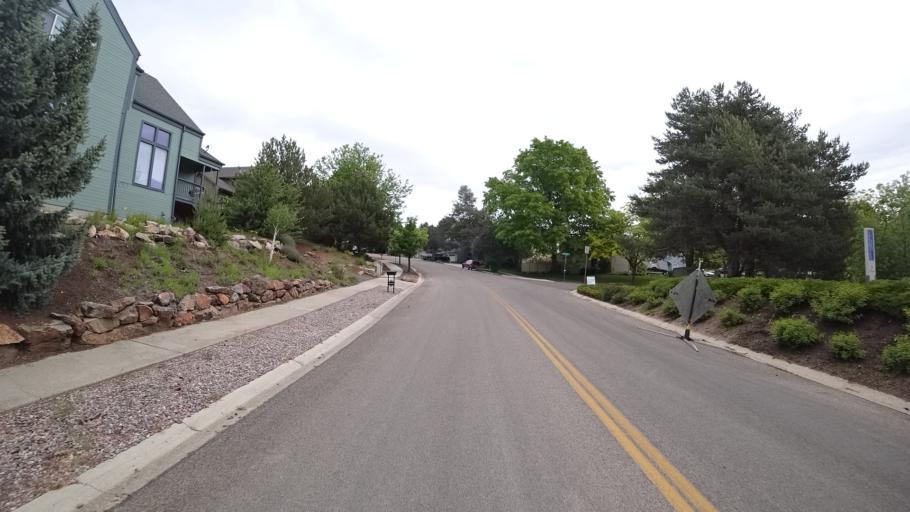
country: US
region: Idaho
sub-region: Ada County
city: Boise
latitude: 43.6122
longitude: -116.1704
